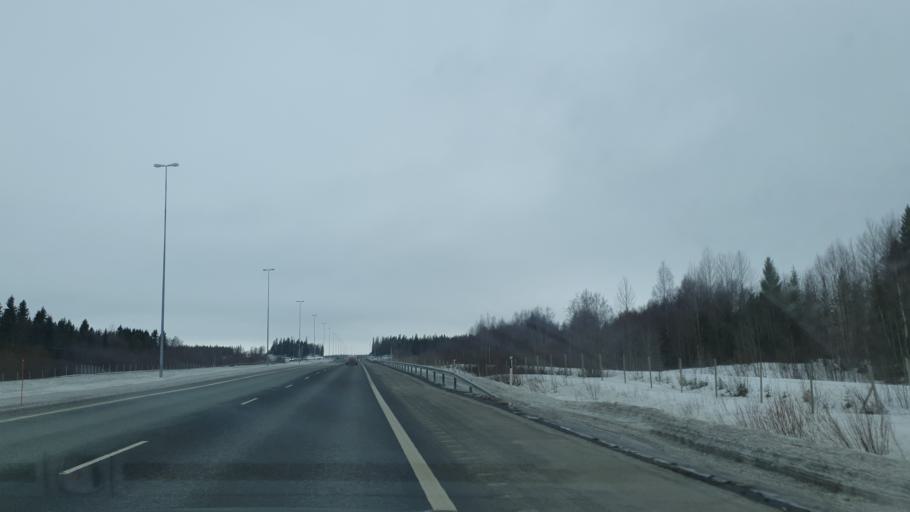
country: FI
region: Lapland
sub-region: Kemi-Tornio
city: Keminmaa
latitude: 65.8260
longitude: 24.4301
